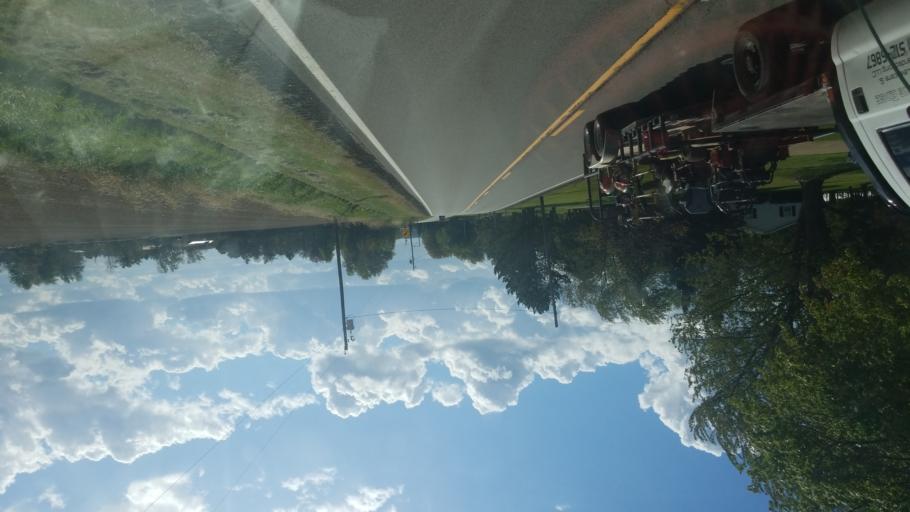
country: US
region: Ohio
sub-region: Richland County
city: Shelby
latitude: 40.8339
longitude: -82.6558
